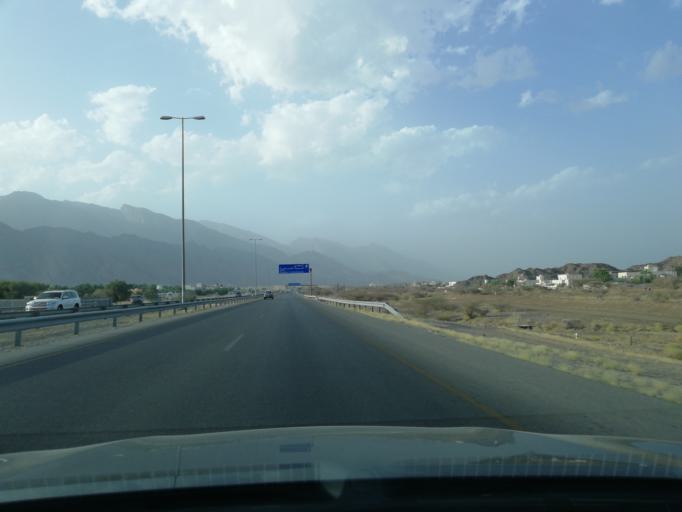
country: OM
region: Muhafazat ad Dakhiliyah
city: Izki
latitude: 22.9886
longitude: 57.7917
